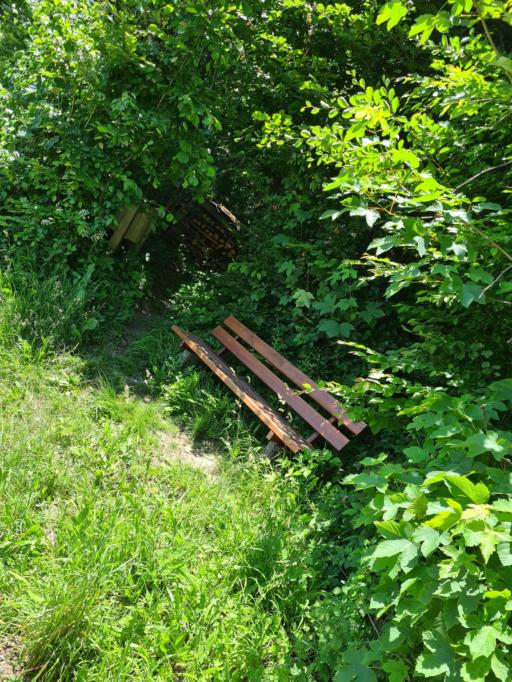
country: AT
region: Salzburg
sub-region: Politischer Bezirk Hallein
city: Oberalm
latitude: 47.7035
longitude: 13.1160
